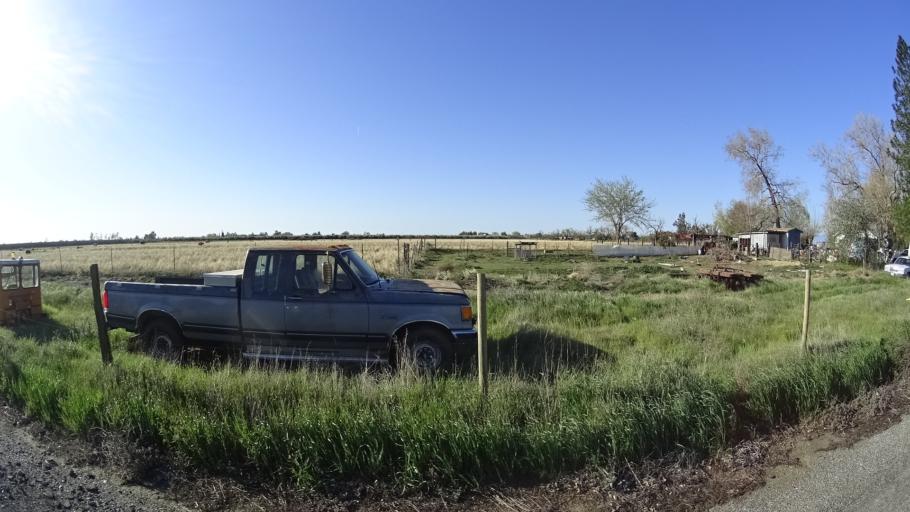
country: US
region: California
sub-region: Glenn County
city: Orland
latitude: 39.7550
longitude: -122.2334
